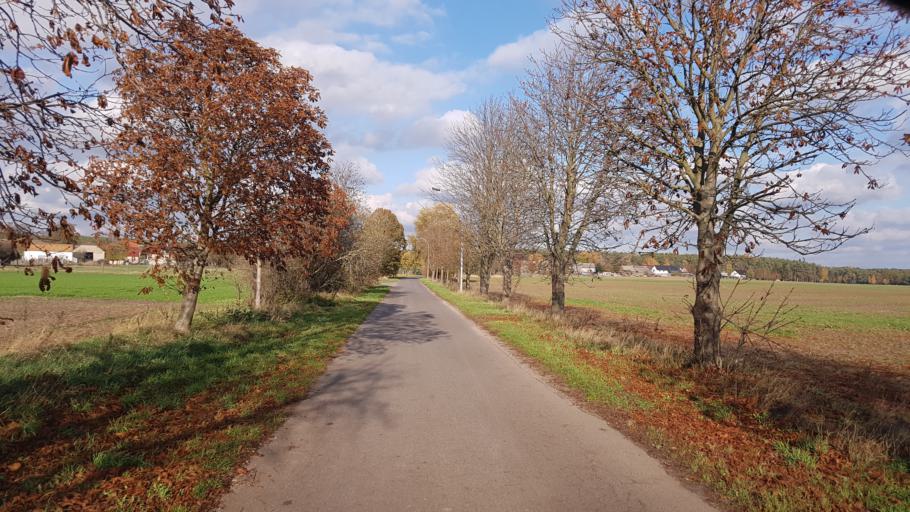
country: DE
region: Brandenburg
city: Schonewalde
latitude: 51.6949
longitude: 13.5722
